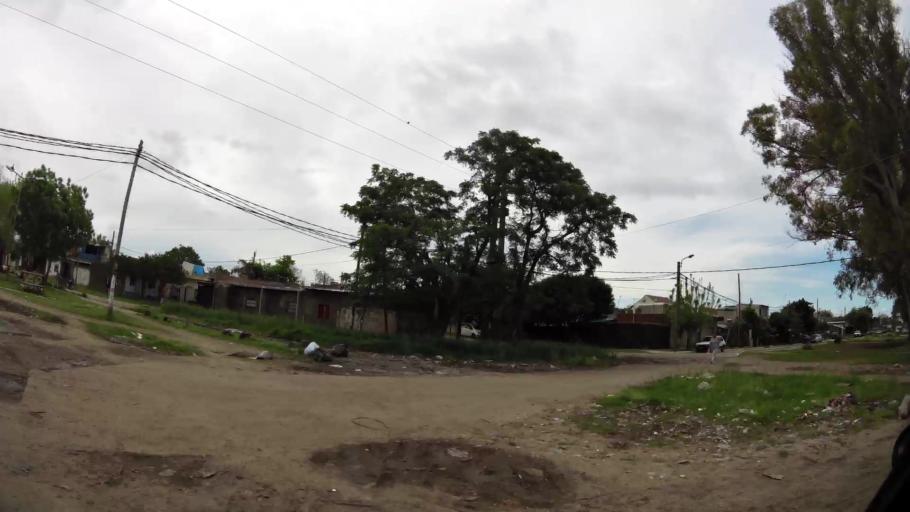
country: AR
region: Buenos Aires
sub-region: Partido de Quilmes
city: Quilmes
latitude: -34.7605
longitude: -58.2599
